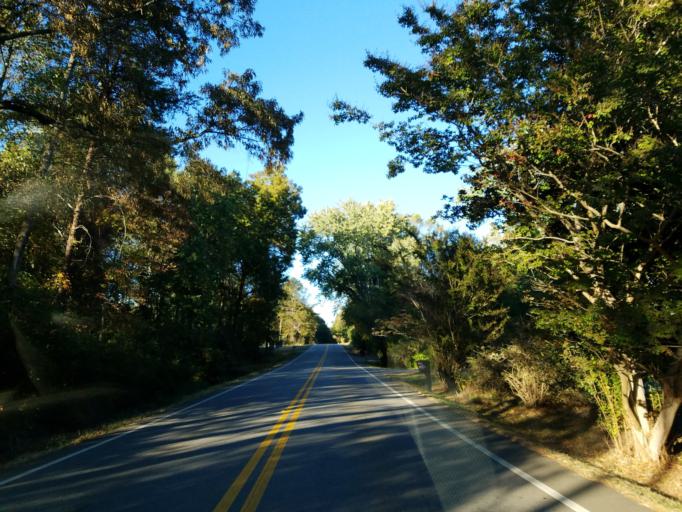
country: US
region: Georgia
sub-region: Dawson County
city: Dawsonville
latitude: 34.4243
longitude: -84.1925
